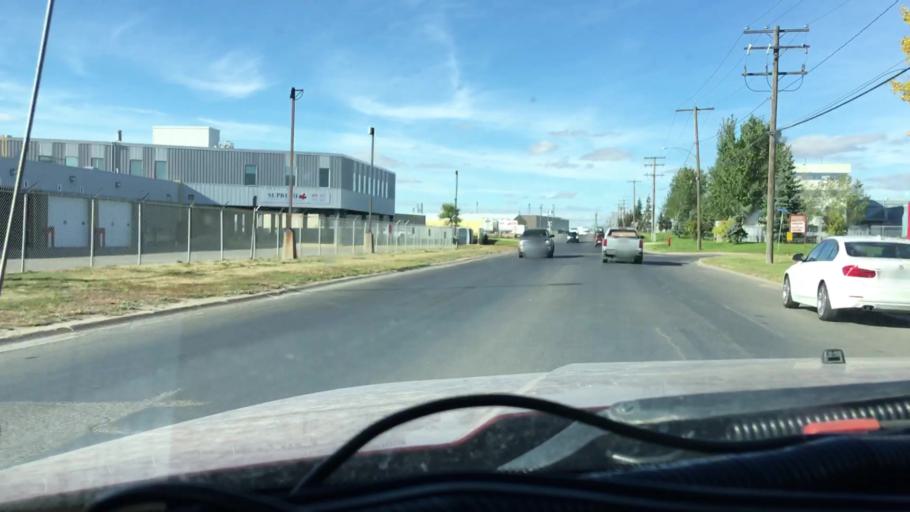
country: CA
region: Saskatchewan
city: Regina
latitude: 50.4721
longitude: -104.5615
